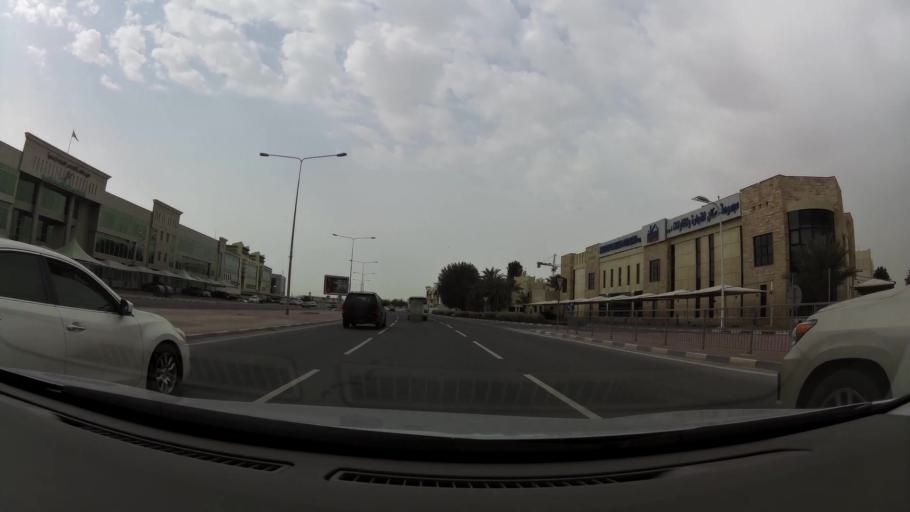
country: QA
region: Baladiyat ad Dawhah
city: Doha
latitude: 25.2973
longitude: 51.4990
